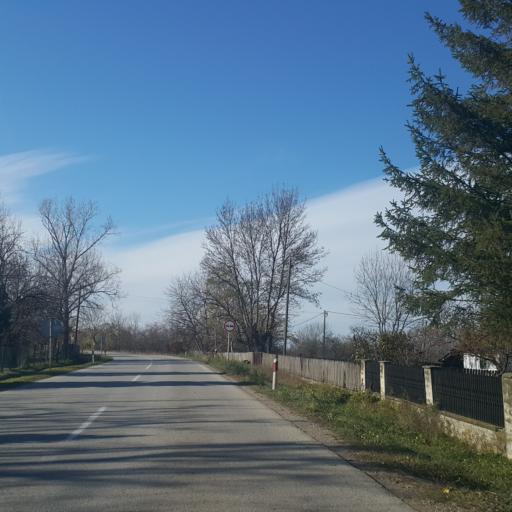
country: RS
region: Central Serbia
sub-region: Sumadijski Okrug
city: Topola
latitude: 44.2504
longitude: 20.7754
